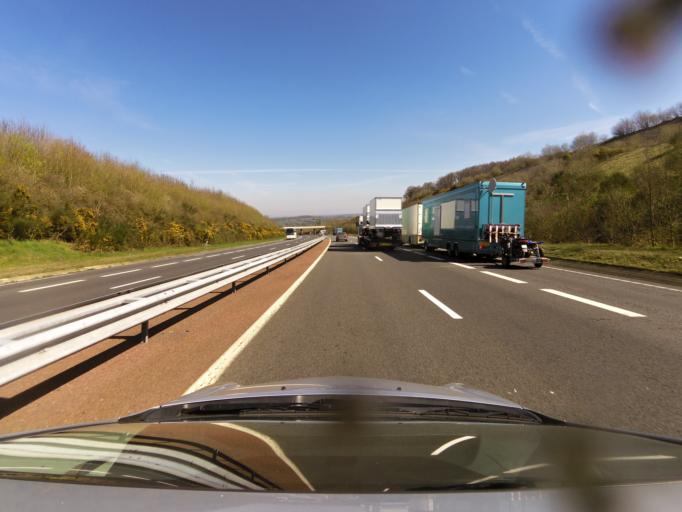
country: FR
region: Lower Normandy
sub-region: Departement de la Manche
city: Tessy-sur-Vire
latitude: 48.9245
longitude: -1.0773
